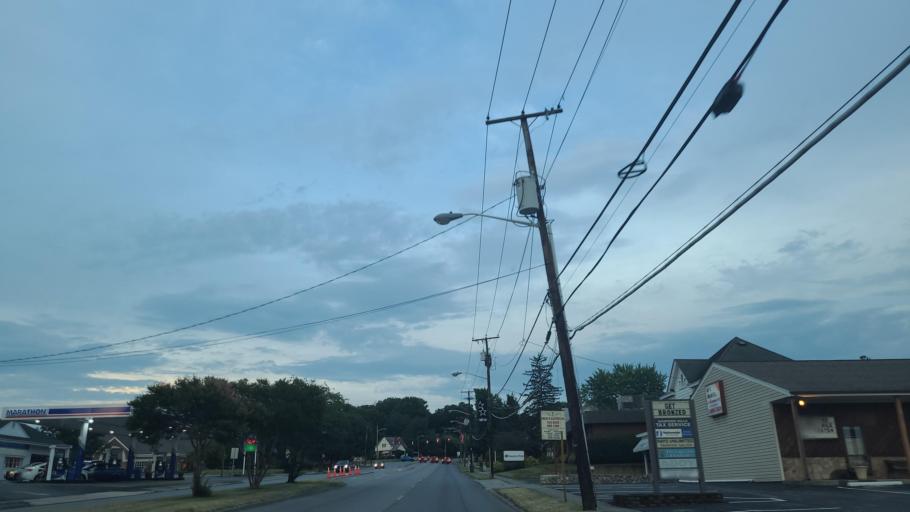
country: US
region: Virginia
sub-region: Roanoke County
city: Vinton
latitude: 37.2762
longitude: -79.9027
